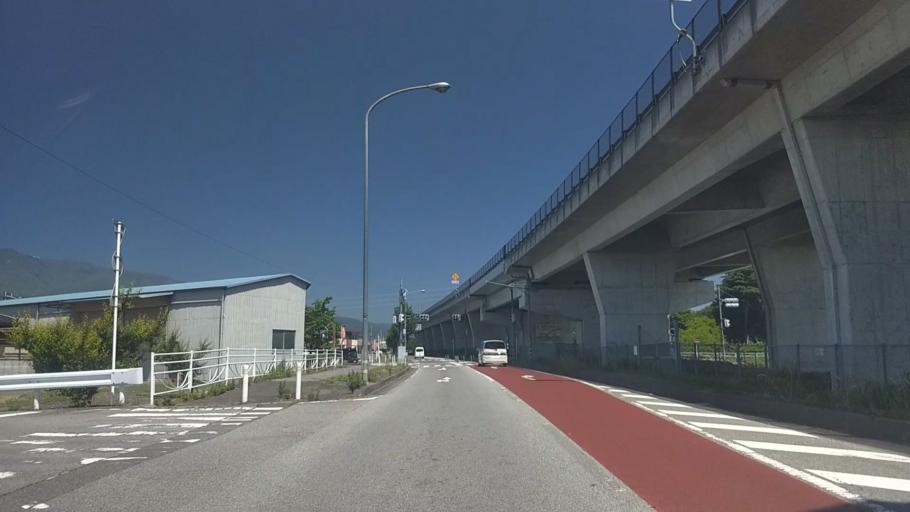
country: JP
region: Yamanashi
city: Ryuo
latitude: 35.6193
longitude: 138.4785
